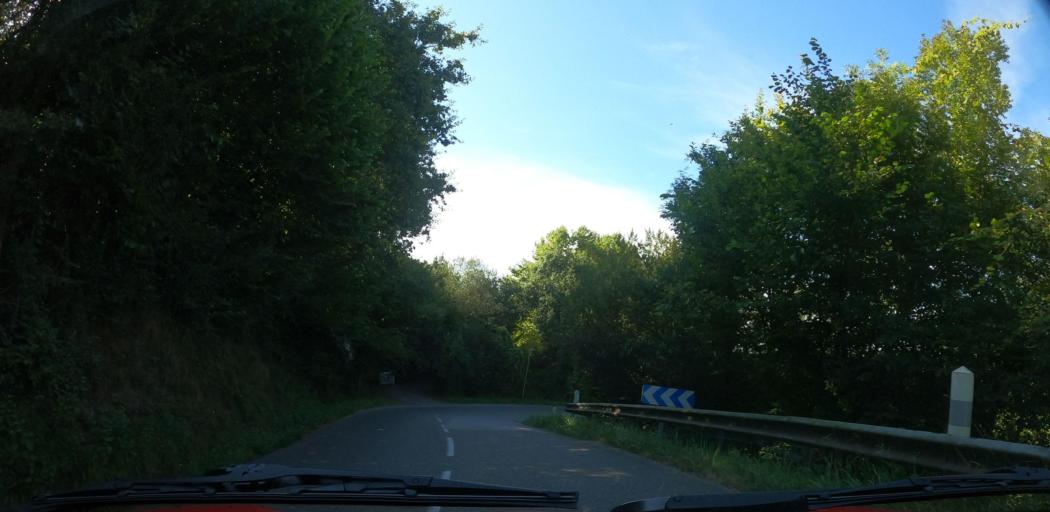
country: FR
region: Aquitaine
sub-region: Departement des Pyrenees-Atlantiques
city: Saint-Pee-sur-Nivelle
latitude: 43.3637
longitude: -1.5452
